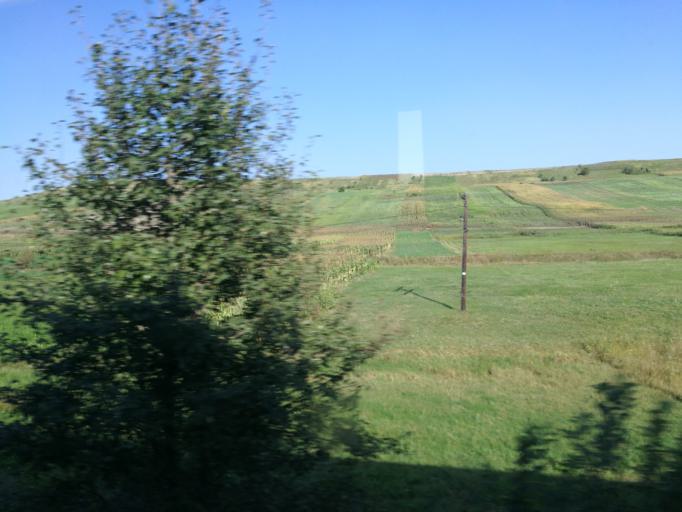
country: RO
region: Vaslui
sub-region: Comuna Rebricea
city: Rebricea
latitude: 46.8652
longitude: 27.5642
